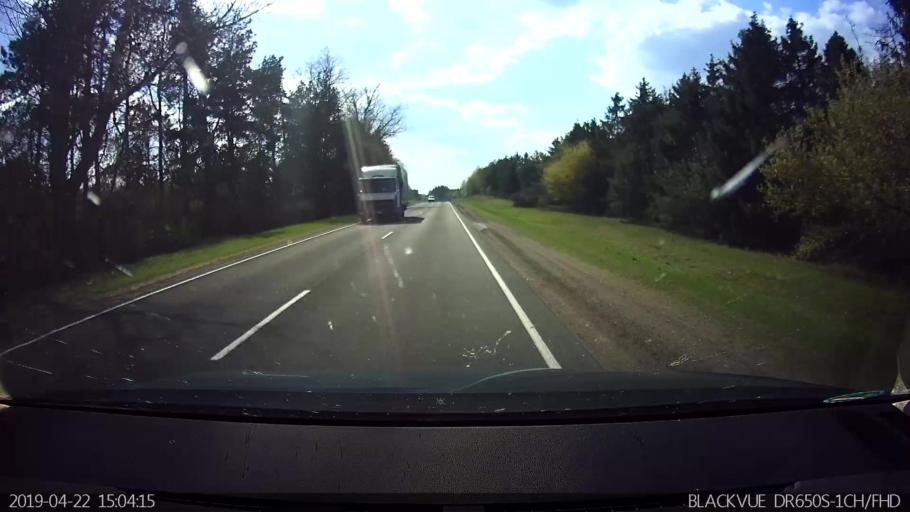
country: BY
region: Brest
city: Kamyanyets
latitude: 52.3409
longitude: 23.9001
